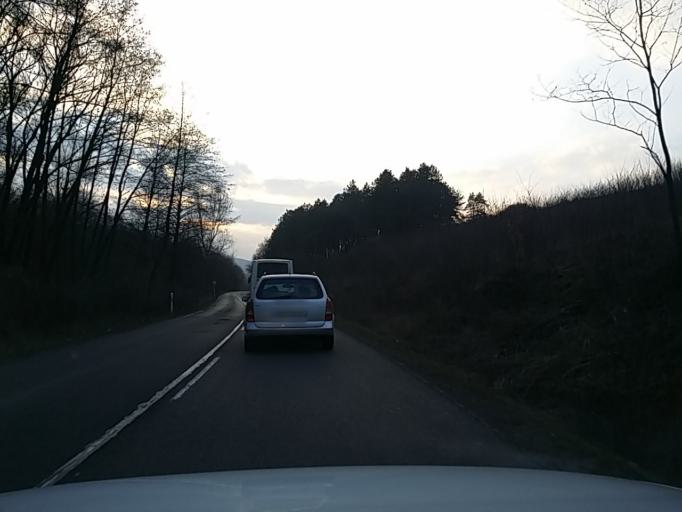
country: HU
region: Nograd
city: Matranovak
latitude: 48.0101
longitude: 19.9853
